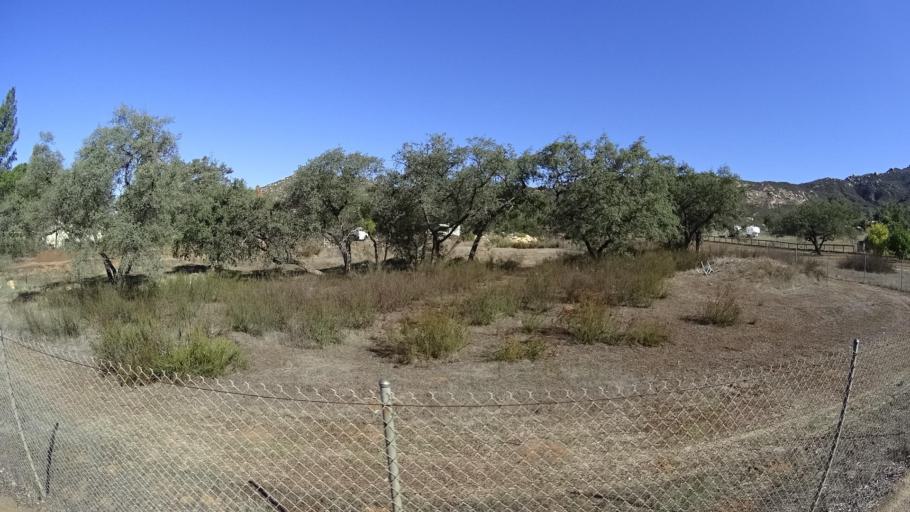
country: US
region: California
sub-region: San Diego County
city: Jamul
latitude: 32.7225
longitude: -116.8080
